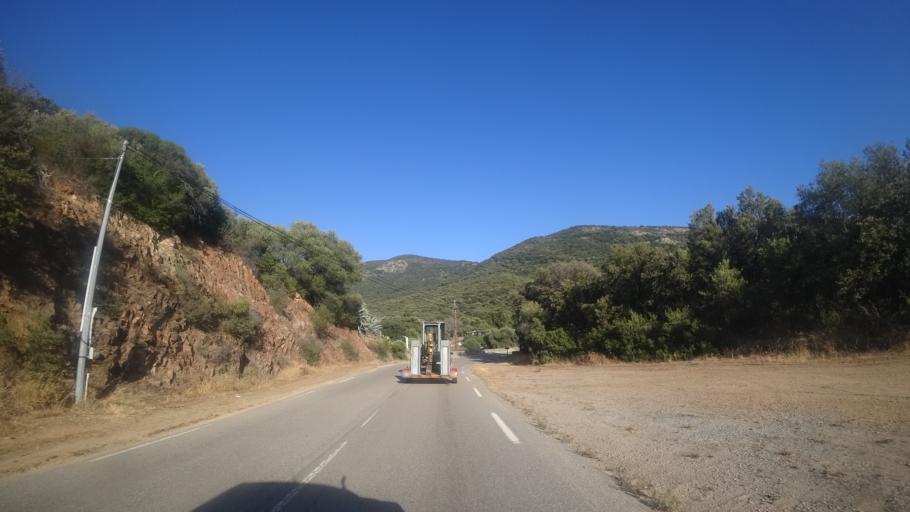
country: FR
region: Corsica
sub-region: Departement de la Corse-du-Sud
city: Cargese
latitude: 42.1557
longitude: 8.6067
